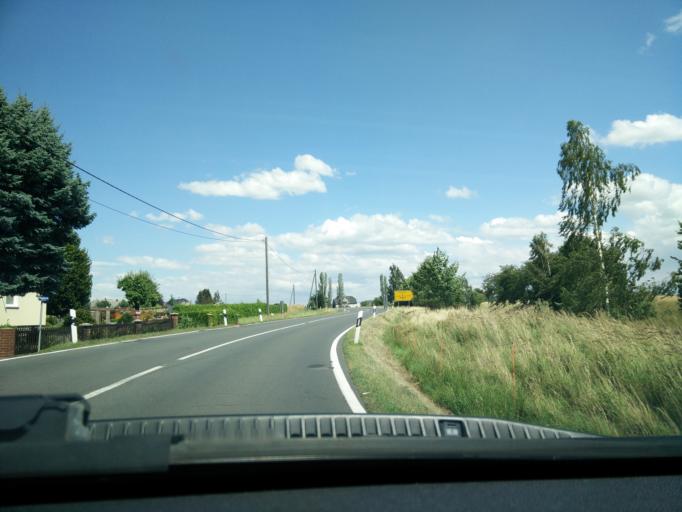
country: DE
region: Saxony
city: Narsdorf
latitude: 51.0155
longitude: 12.7283
